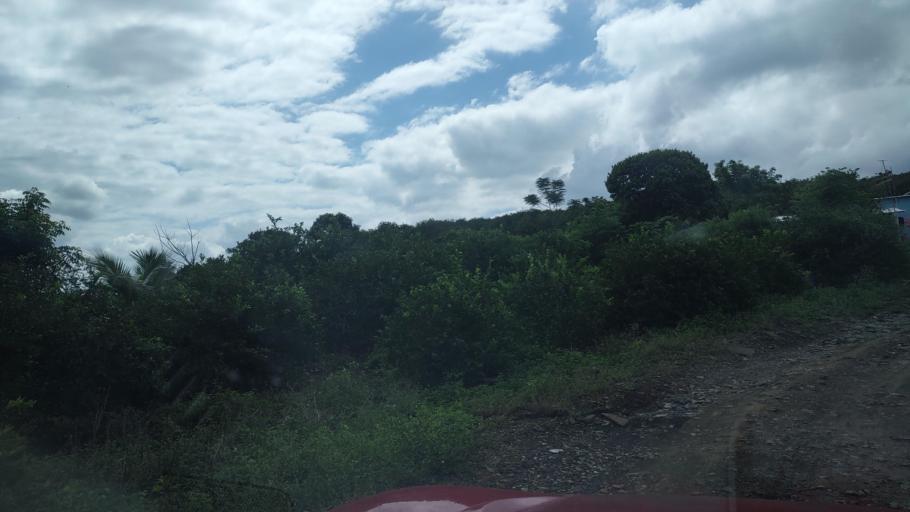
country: MX
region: Puebla
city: San Jose Acateno
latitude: 20.2240
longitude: -97.1580
